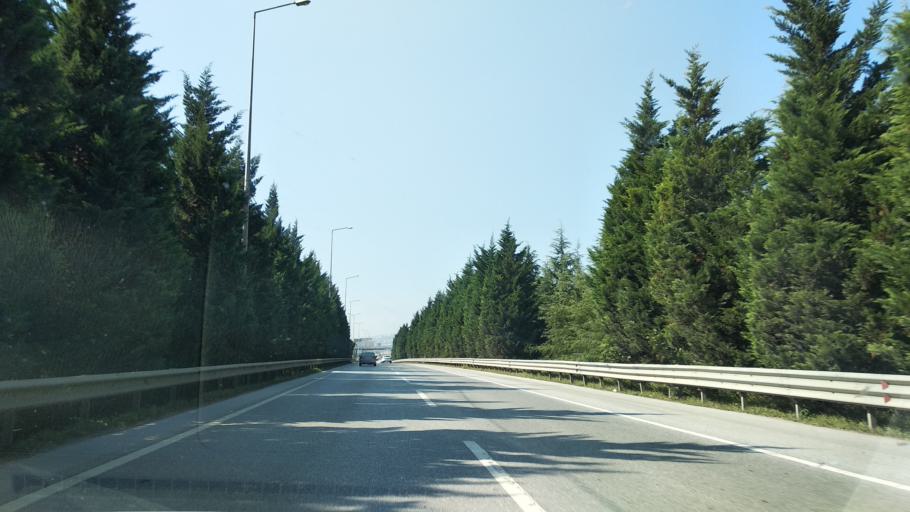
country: TR
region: Kocaeli
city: Kosekoy
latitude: 40.7558
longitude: 30.0075
